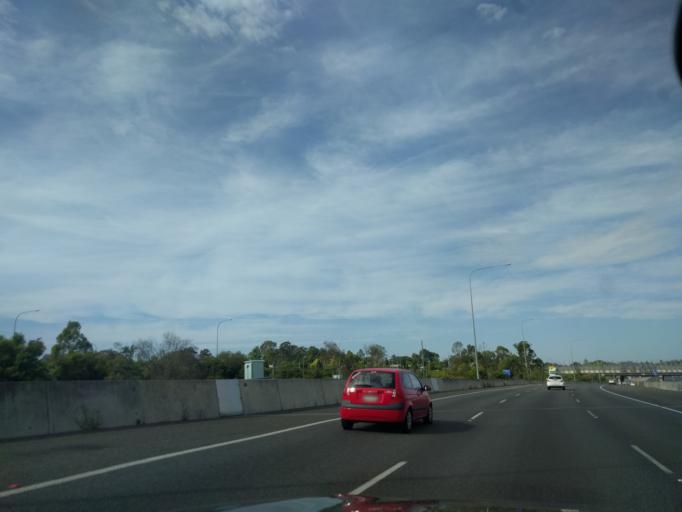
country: AU
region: Queensland
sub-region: Brisbane
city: Wacol
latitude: -27.6047
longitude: 152.9178
